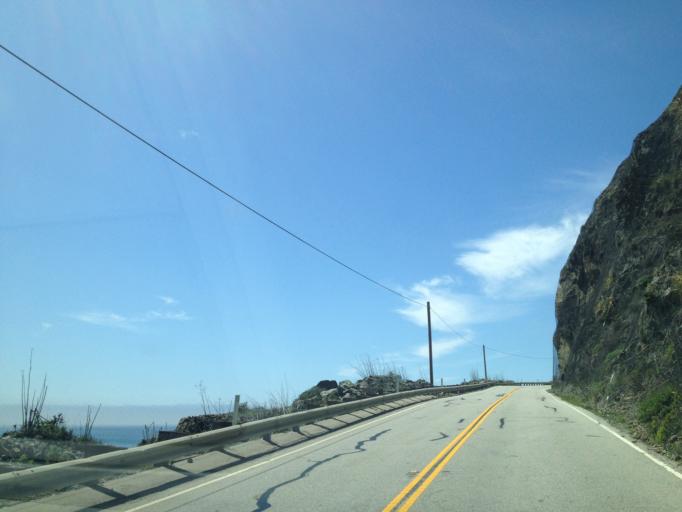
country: US
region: California
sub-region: Monterey County
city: Greenfield
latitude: 36.0097
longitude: -121.5213
